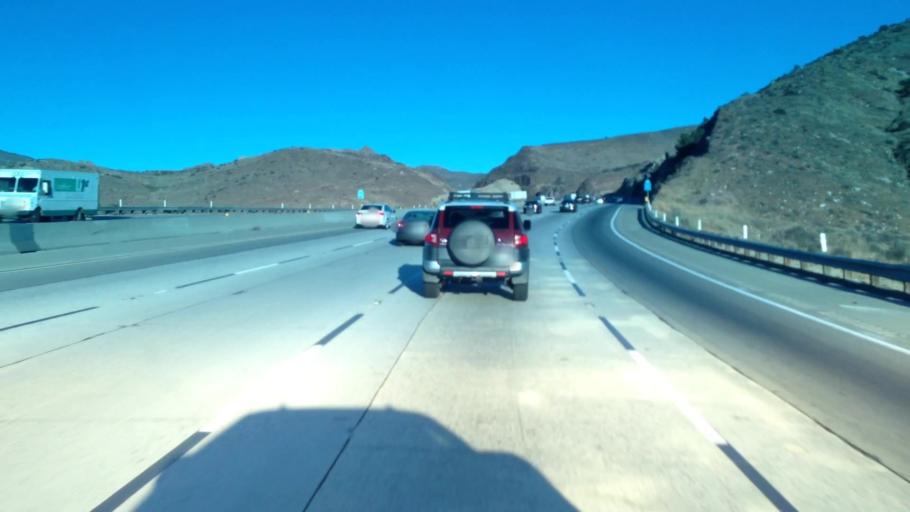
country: US
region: California
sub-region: Los Angeles County
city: Agua Dulce
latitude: 34.4717
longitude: -118.3170
